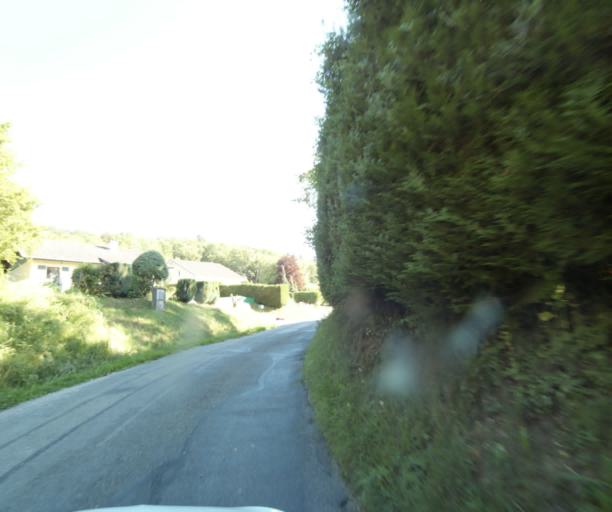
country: FR
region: Rhone-Alpes
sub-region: Departement de la Haute-Savoie
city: Massongy
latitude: 46.3136
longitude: 6.3366
